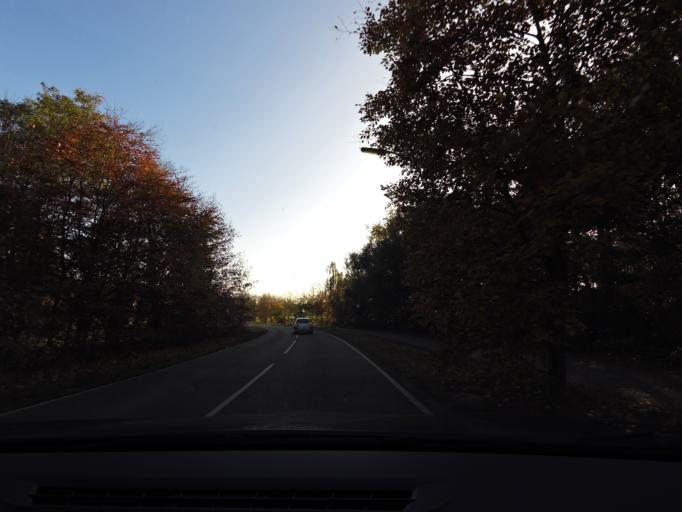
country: NL
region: North Brabant
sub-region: Gemeente Breda
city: Breda
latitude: 51.5259
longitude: 4.7692
